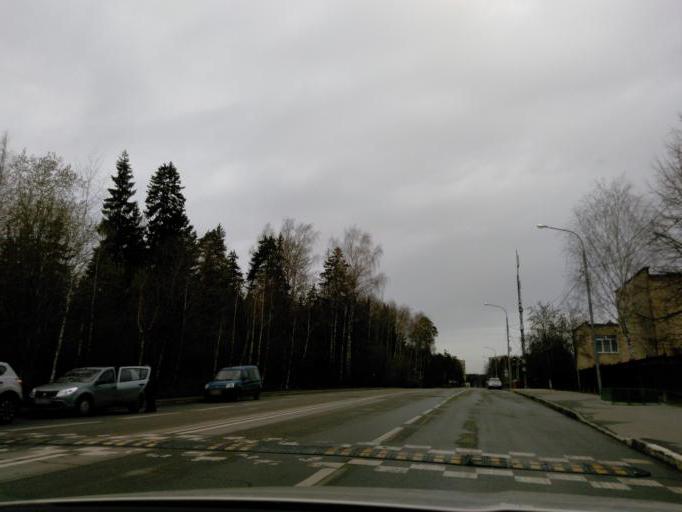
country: RU
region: Moskovskaya
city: Rzhavki
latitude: 55.9930
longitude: 37.2460
